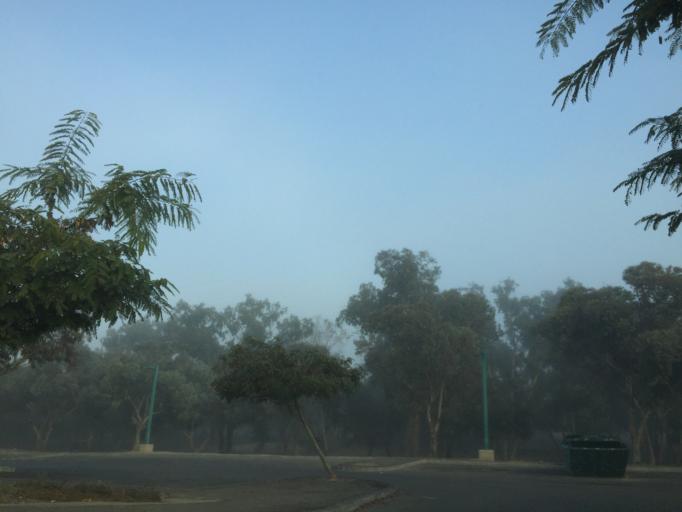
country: IL
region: Southern District
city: Yeroham
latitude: 30.9898
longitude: 34.9123
